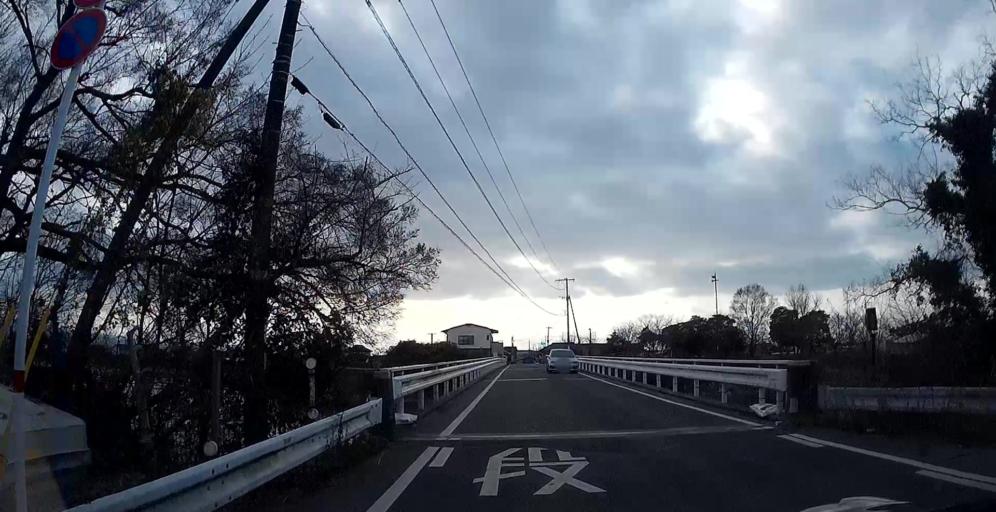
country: JP
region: Kumamoto
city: Yatsushiro
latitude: 32.5523
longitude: 130.6217
